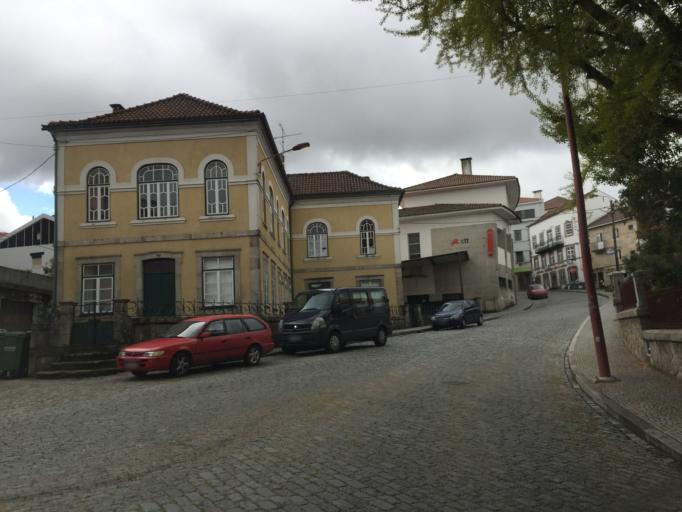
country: PT
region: Guarda
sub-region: Manteigas
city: Manteigas
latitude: 40.4955
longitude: -7.5926
